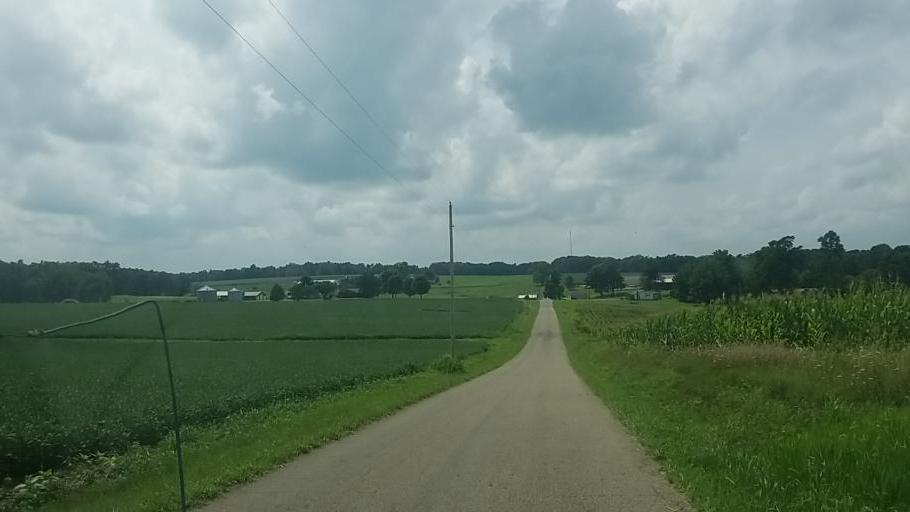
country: US
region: Ohio
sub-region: Knox County
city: Gambier
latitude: 40.2614
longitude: -82.2988
